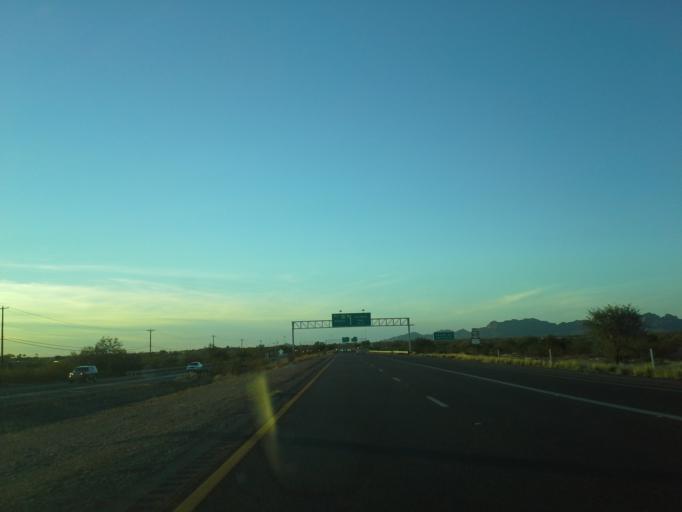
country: US
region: Arizona
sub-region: Pinal County
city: Apache Junction
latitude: 33.3834
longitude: -111.4956
